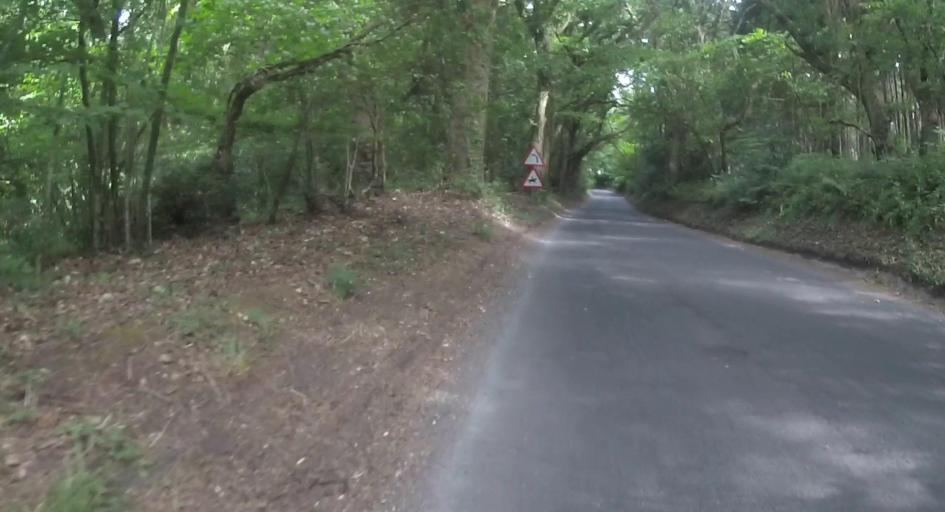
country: GB
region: England
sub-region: Dorset
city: Wool
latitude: 50.6712
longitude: -2.1730
